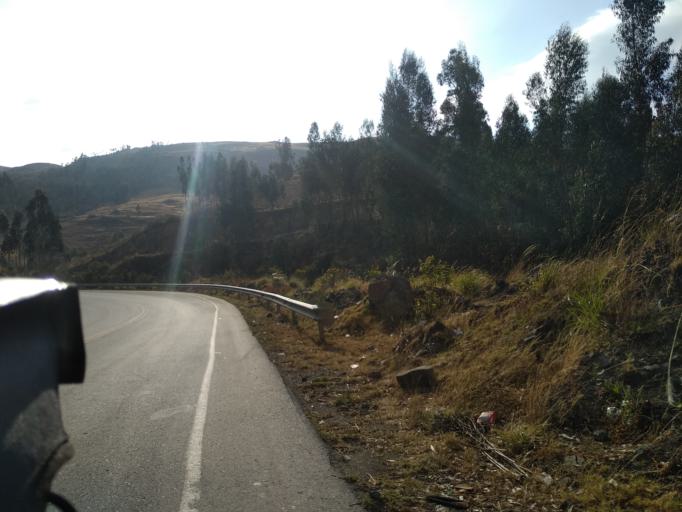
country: PE
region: La Libertad
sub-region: Provincia de Otuzco
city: Agallpampa
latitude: -7.9943
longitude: -78.5289
